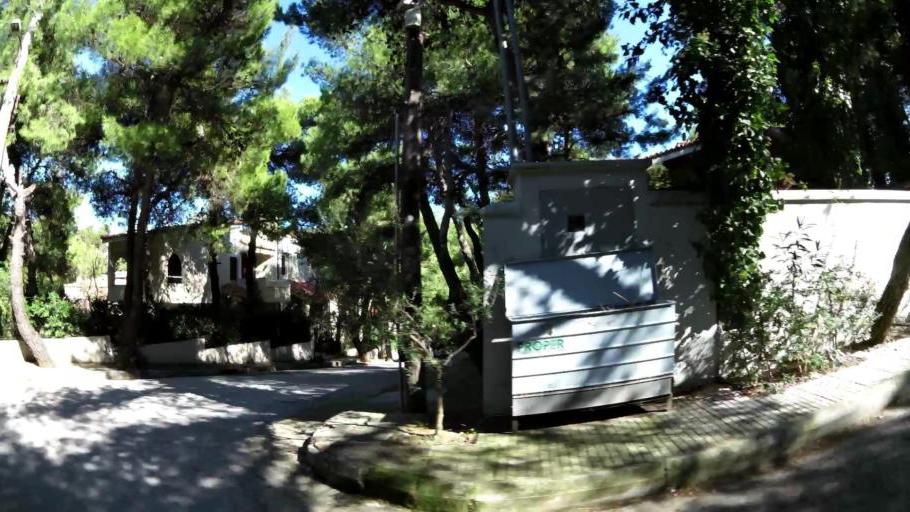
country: GR
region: Attica
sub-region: Nomarchia Anatolikis Attikis
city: Dionysos
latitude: 38.1041
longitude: 23.8870
